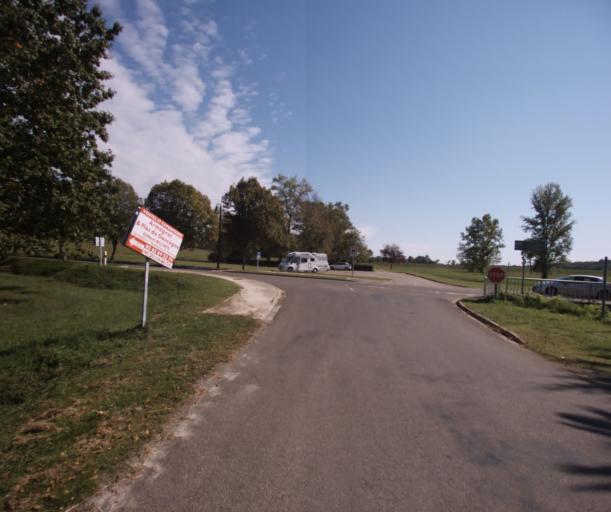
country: FR
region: Midi-Pyrenees
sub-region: Departement du Gers
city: Cazaubon
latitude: 43.9429
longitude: -0.0534
